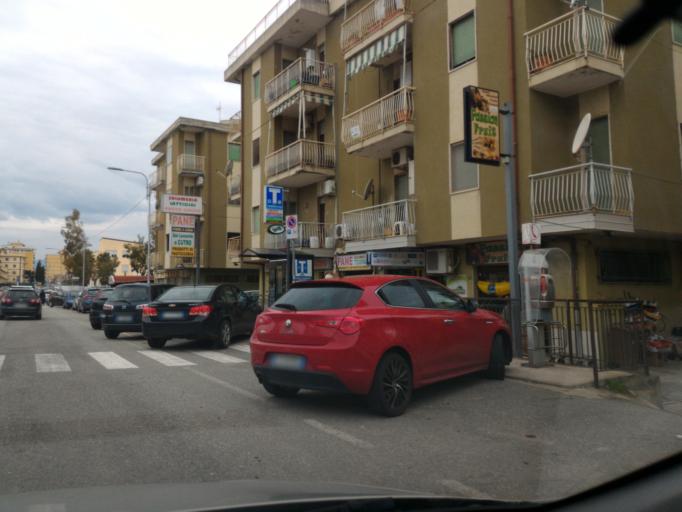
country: IT
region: Calabria
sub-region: Provincia di Catanzaro
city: Barone
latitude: 38.8309
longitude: 16.6288
